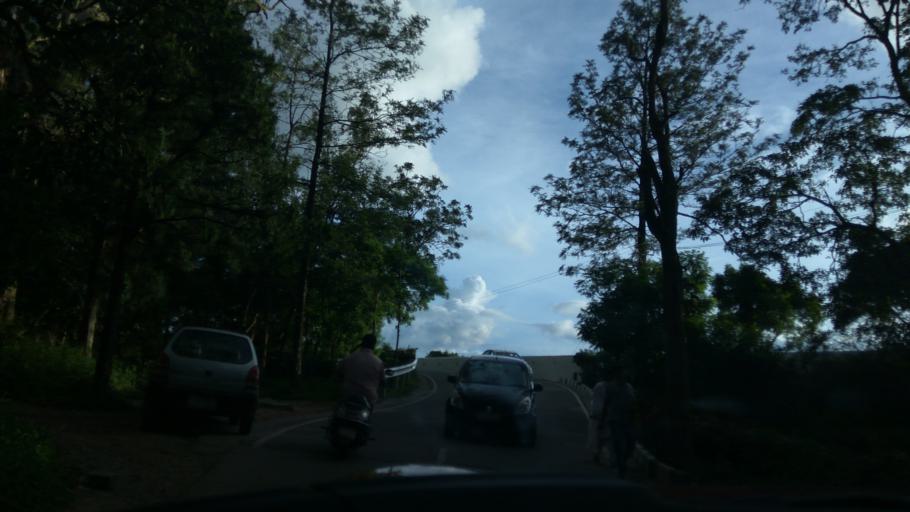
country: IN
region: Karnataka
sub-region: Chikkaballapur
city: Chik Ballapur
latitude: 13.3710
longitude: 77.6805
